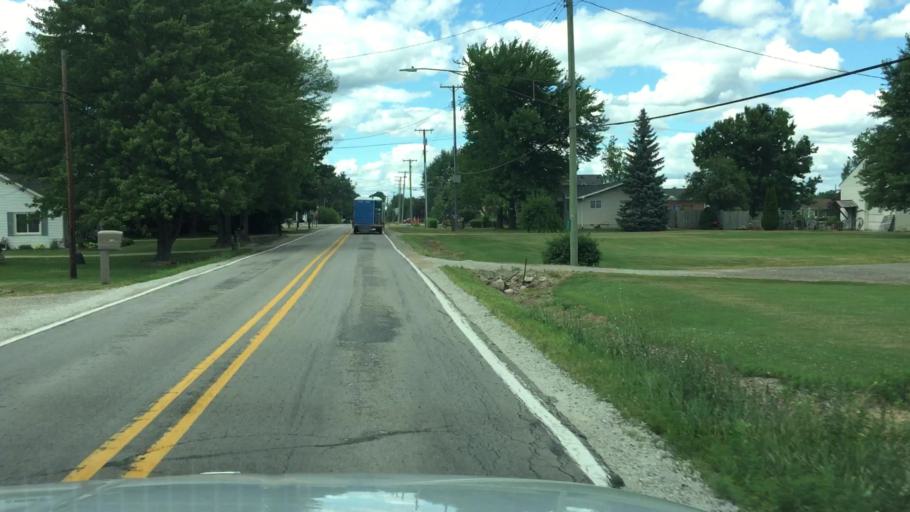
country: US
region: Michigan
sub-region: Saint Clair County
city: Capac
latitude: 42.9222
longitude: -82.9456
